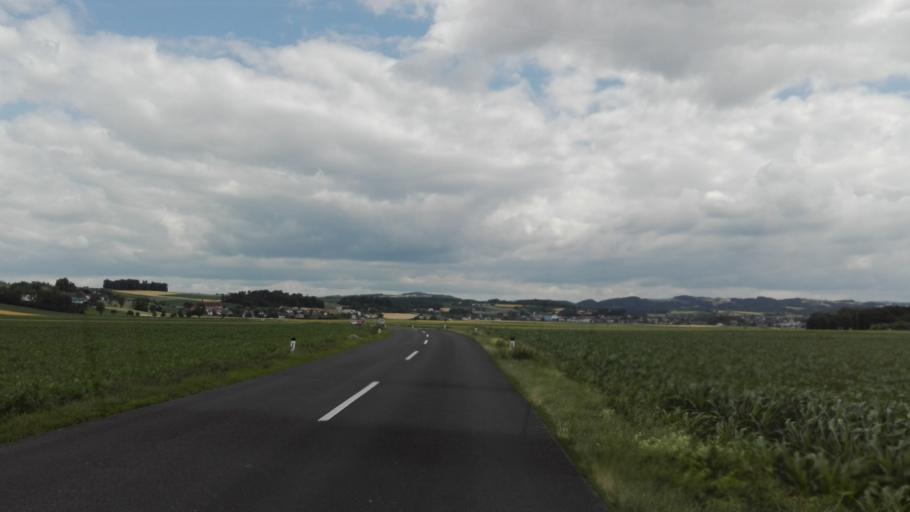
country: AT
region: Lower Austria
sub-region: Politischer Bezirk Amstetten
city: Ennsdorf
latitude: 48.2532
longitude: 14.5433
